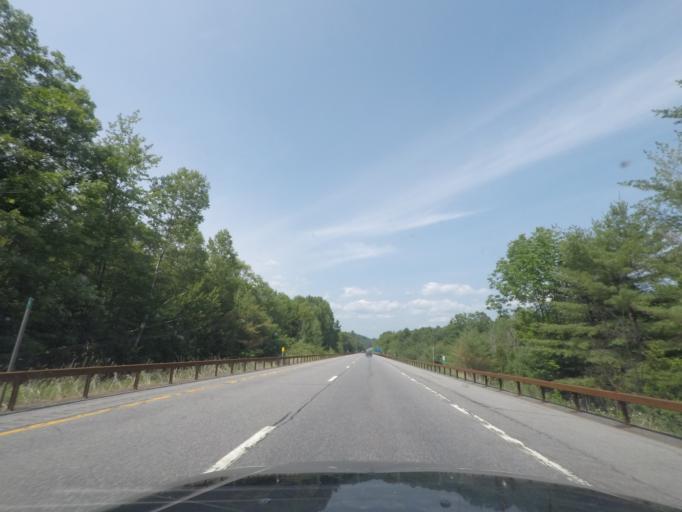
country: US
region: New York
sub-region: Warren County
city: Warrensburg
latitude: 43.7693
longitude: -73.8020
